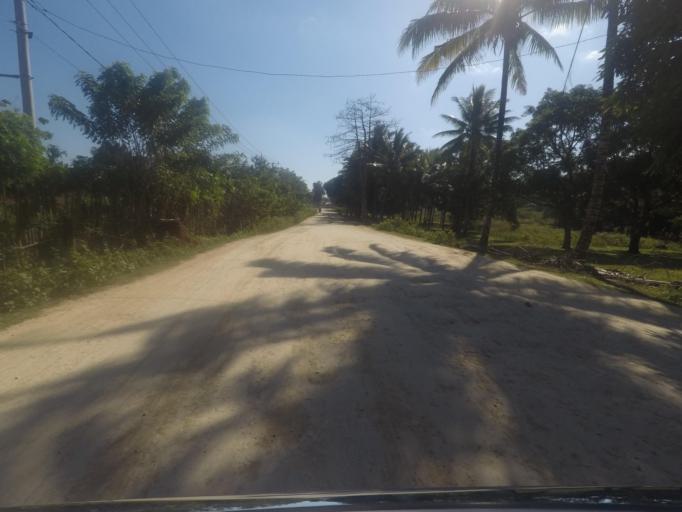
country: TL
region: Lautem
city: Lospalos
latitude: -8.5078
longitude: 126.9915
